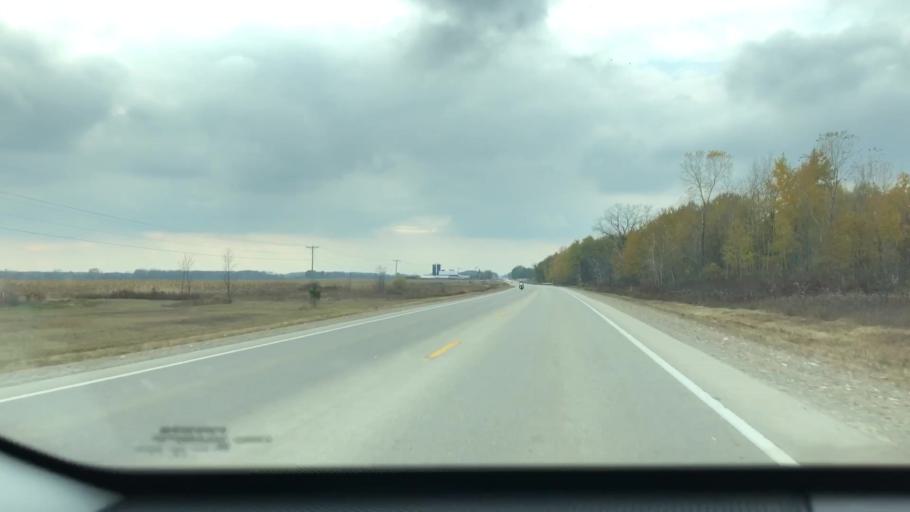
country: US
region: Wisconsin
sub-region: Brown County
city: Oneida
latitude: 44.5024
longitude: -88.2398
